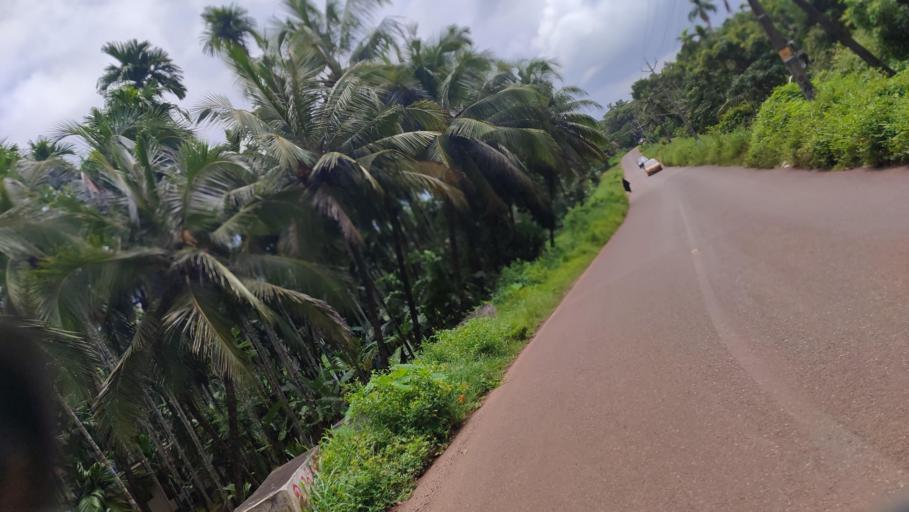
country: IN
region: Kerala
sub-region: Kasaragod District
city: Kannangad
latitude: 12.3958
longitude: 75.0539
